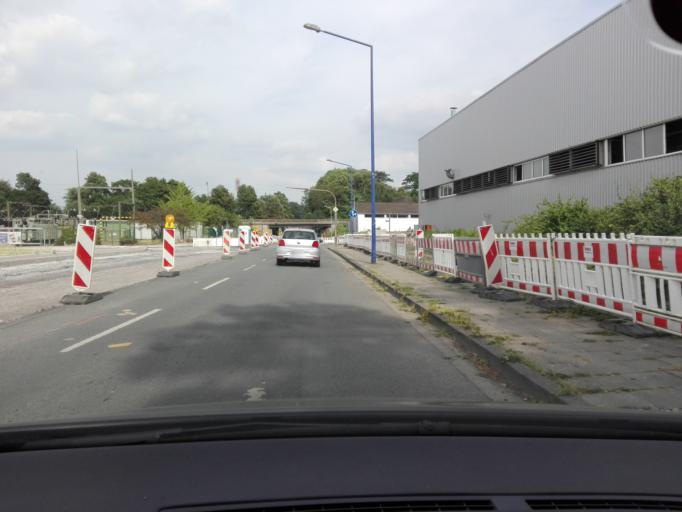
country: DE
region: North Rhine-Westphalia
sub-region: Regierungsbezirk Arnsberg
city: Unna
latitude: 51.5413
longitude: 7.6681
